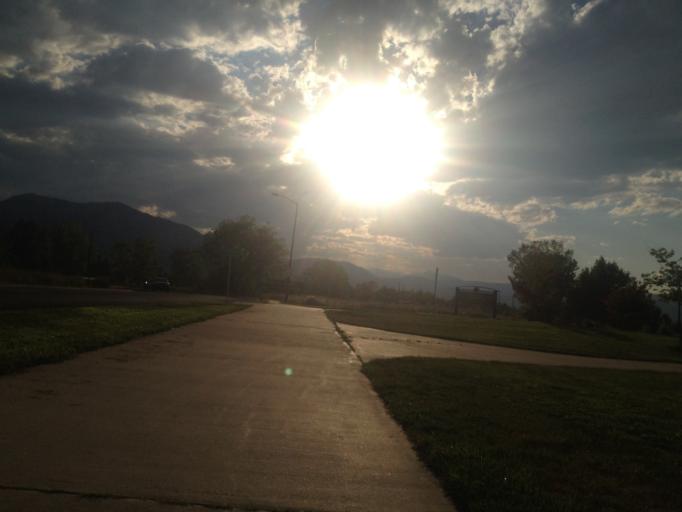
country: US
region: Colorado
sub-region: Boulder County
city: Boulder
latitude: 39.9901
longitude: -105.2217
